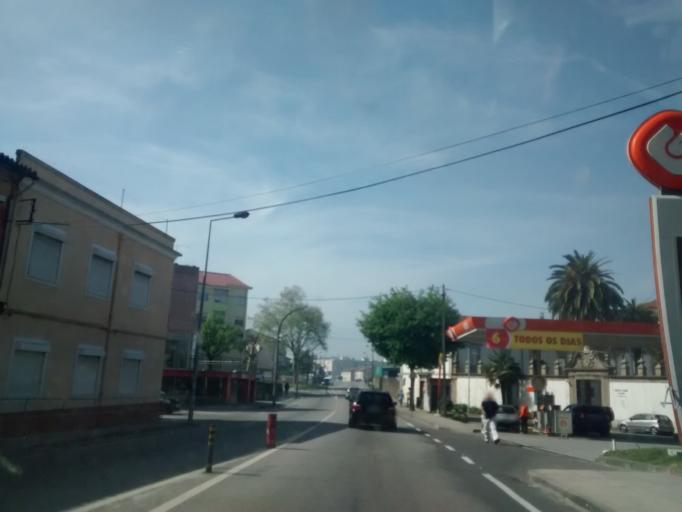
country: PT
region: Braga
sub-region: Braga
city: Braga
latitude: 41.5430
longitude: -8.4353
